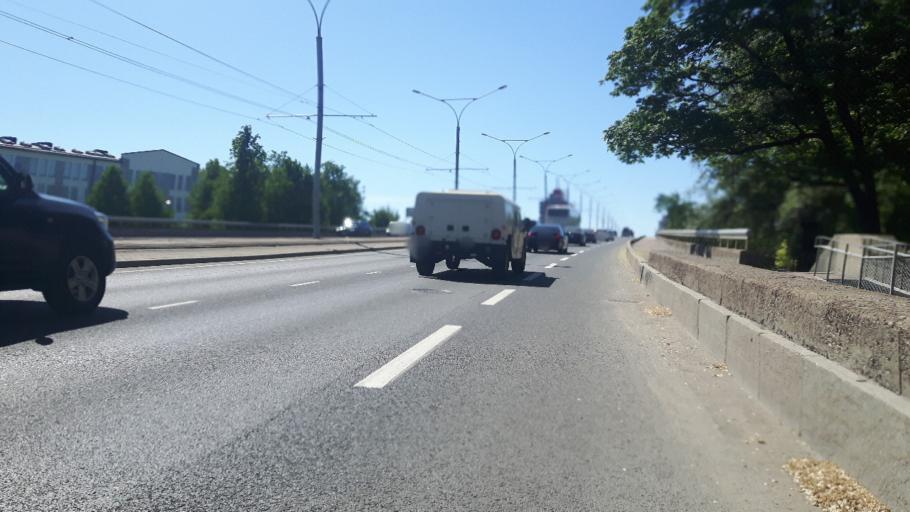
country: EE
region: Harju
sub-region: Tallinna linn
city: Tallinn
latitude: 59.4216
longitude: 24.7423
